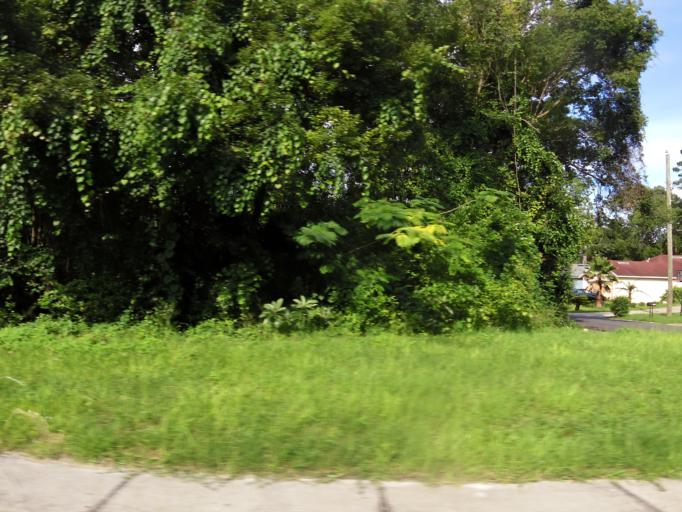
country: US
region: Florida
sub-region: Clay County
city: Green Cove Springs
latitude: 29.9924
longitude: -81.6987
